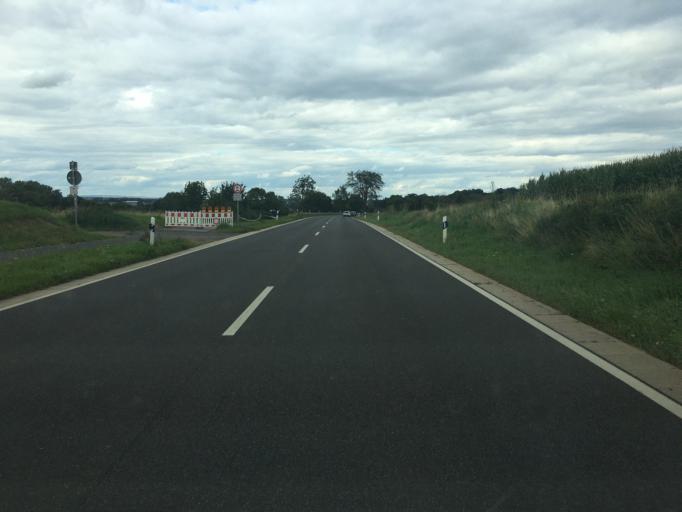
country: DE
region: North Rhine-Westphalia
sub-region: Regierungsbezirk Koln
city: Mechernich
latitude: 50.6352
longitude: 6.6540
